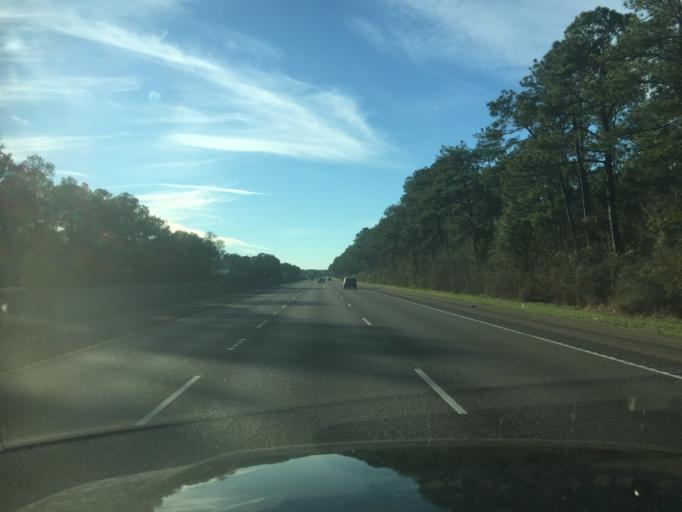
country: US
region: Louisiana
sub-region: Saint Tammany Parish
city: Slidell
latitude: 30.3103
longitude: -89.7972
